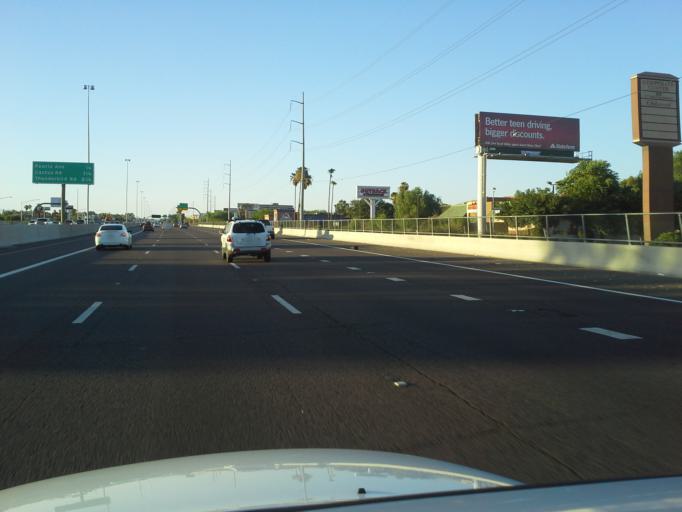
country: US
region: Arizona
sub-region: Maricopa County
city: Glendale
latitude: 33.5743
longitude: -112.1168
